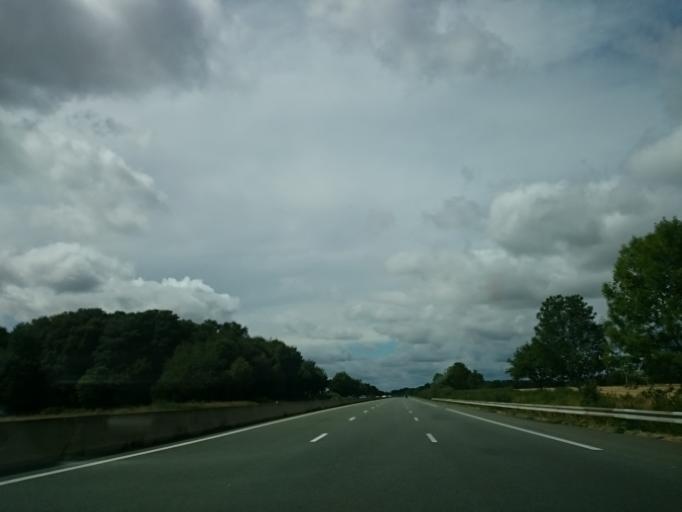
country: FR
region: Centre
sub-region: Departement d'Eure-et-Loir
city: Thiron Gardais
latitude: 48.2284
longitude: 1.0015
